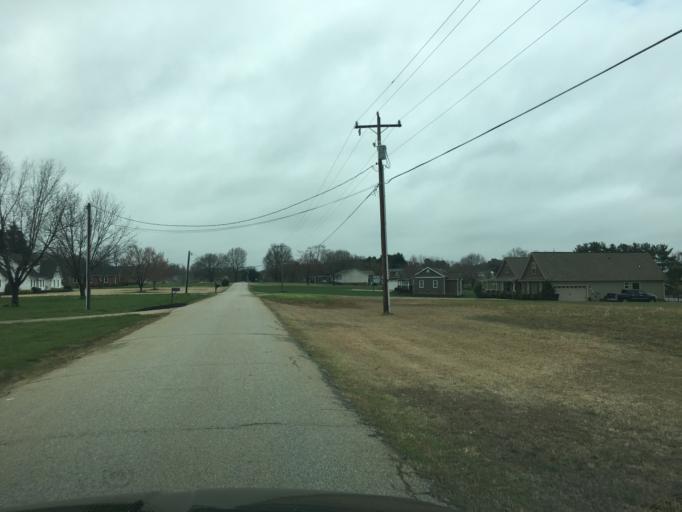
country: US
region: South Carolina
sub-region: Spartanburg County
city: Inman Mills
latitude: 35.0255
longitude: -82.1142
